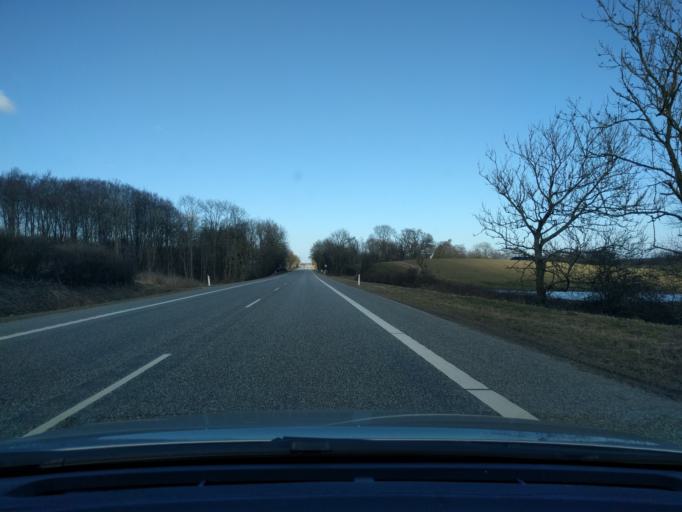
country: DK
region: South Denmark
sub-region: Aabenraa Kommune
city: Lojt Kirkeby
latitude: 55.1502
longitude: 9.4390
